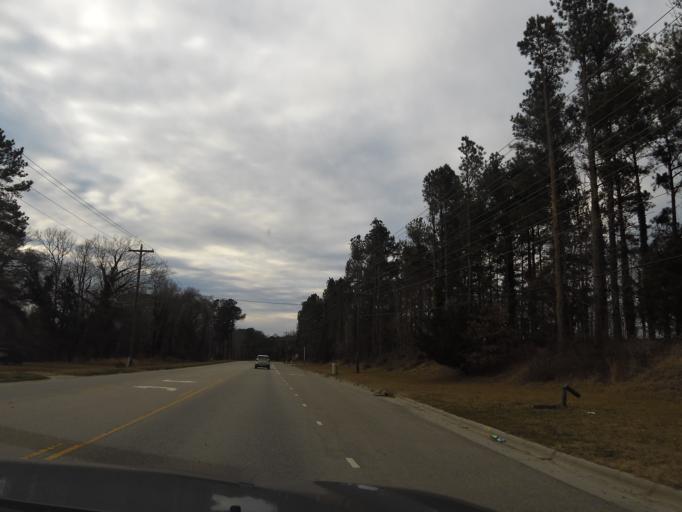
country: US
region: North Carolina
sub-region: Nash County
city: Rocky Mount
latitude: 35.9773
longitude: -77.7503
